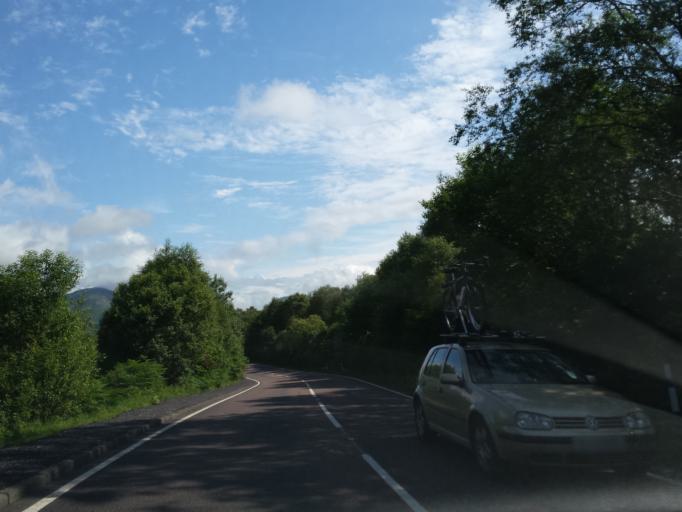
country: GB
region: Scotland
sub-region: Argyll and Bute
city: Garelochhead
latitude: 56.4054
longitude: -5.0354
